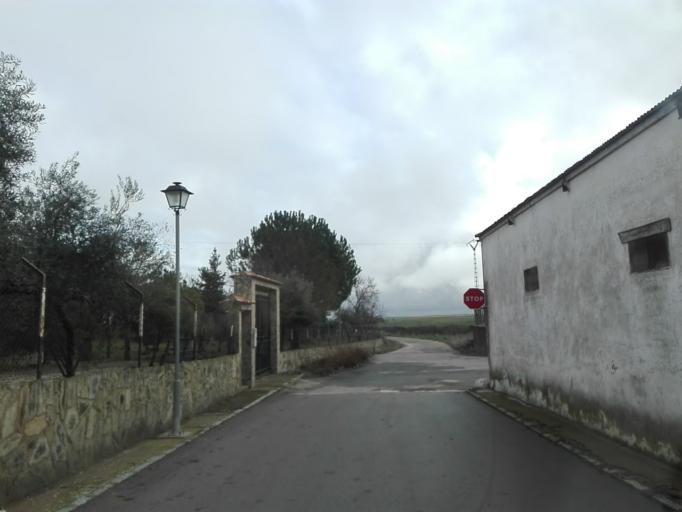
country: ES
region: Extremadura
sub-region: Provincia de Badajoz
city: Villagarcia de la Torre
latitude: 38.2963
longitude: -6.0764
